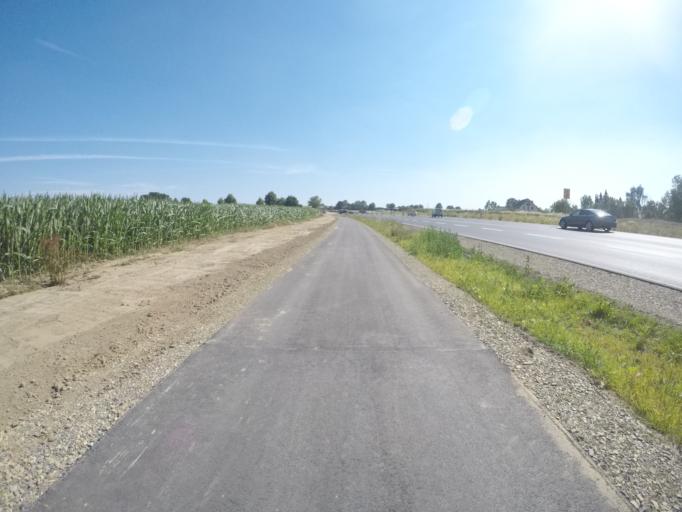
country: DE
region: North Rhine-Westphalia
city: Loehne
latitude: 52.1749
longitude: 8.7496
